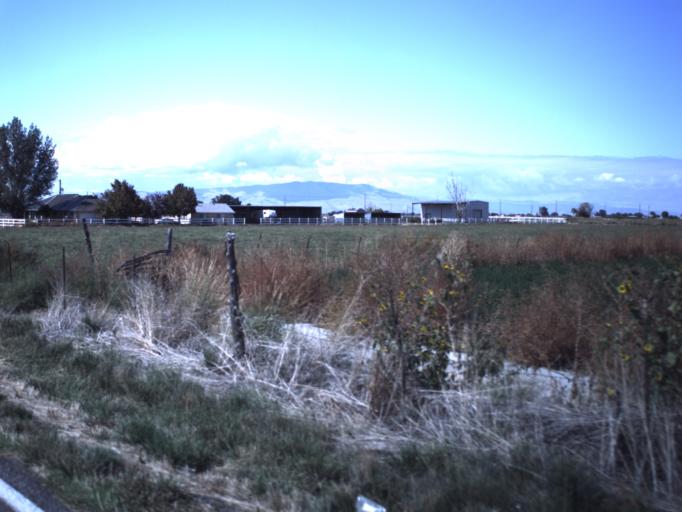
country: US
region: Utah
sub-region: Utah County
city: Spanish Fork
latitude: 40.1155
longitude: -111.6741
